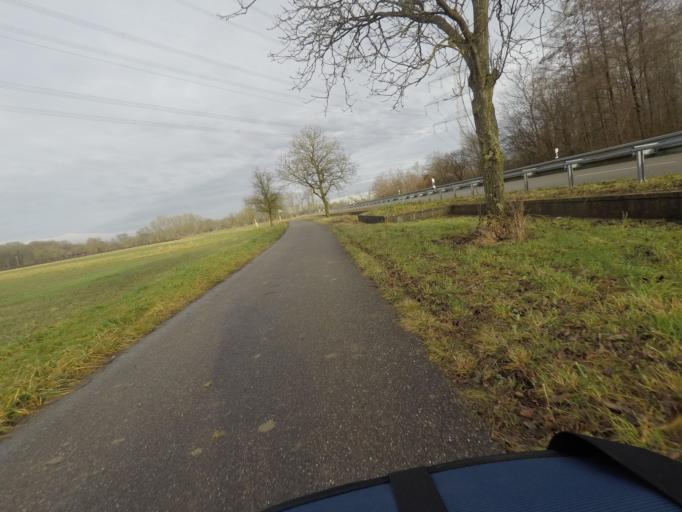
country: DE
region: Baden-Wuerttemberg
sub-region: Karlsruhe Region
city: Steinmauern
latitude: 48.9197
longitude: 8.2054
